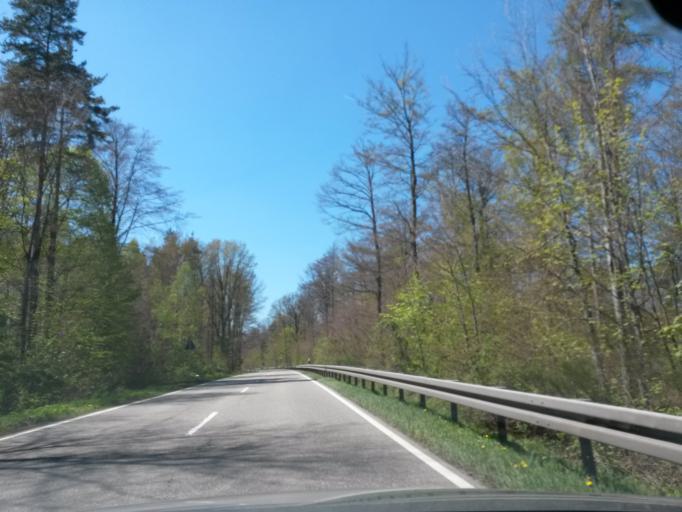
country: DE
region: Baden-Wuerttemberg
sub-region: Karlsruhe Region
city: Neuenburg
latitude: 48.8550
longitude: 8.5932
